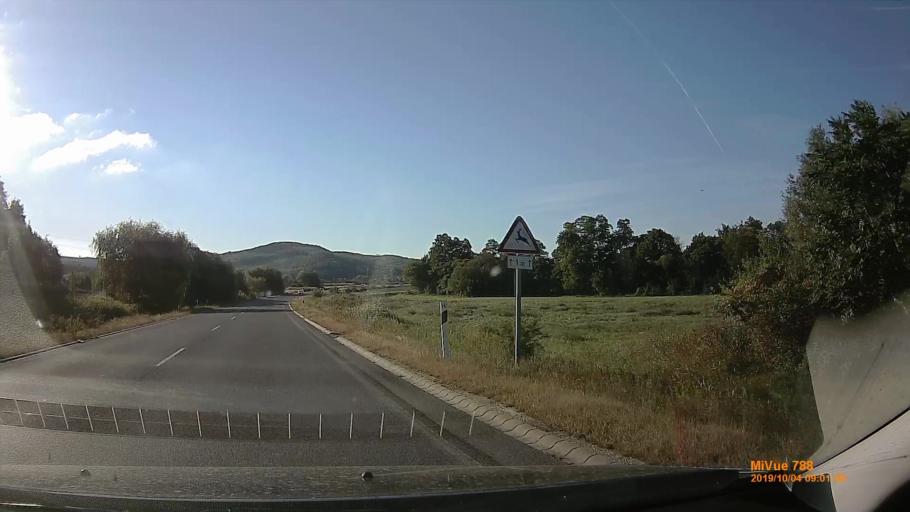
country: HU
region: Somogy
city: Karad
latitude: 46.7371
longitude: 17.7755
